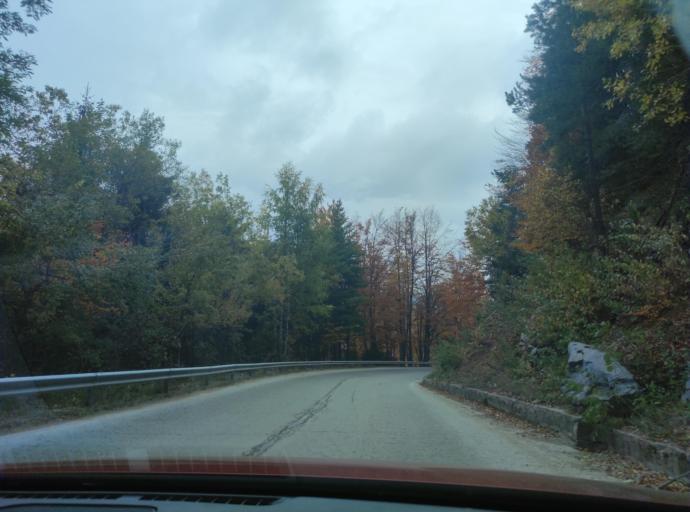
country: BG
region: Montana
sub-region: Obshtina Berkovitsa
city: Berkovitsa
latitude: 43.1332
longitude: 23.1459
